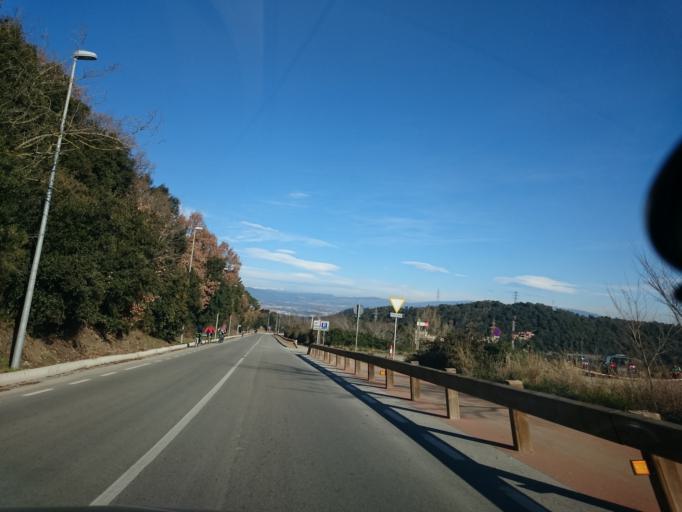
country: ES
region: Catalonia
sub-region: Provincia de Barcelona
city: Sarria-Sant Gervasi
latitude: 41.4268
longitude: 2.1231
